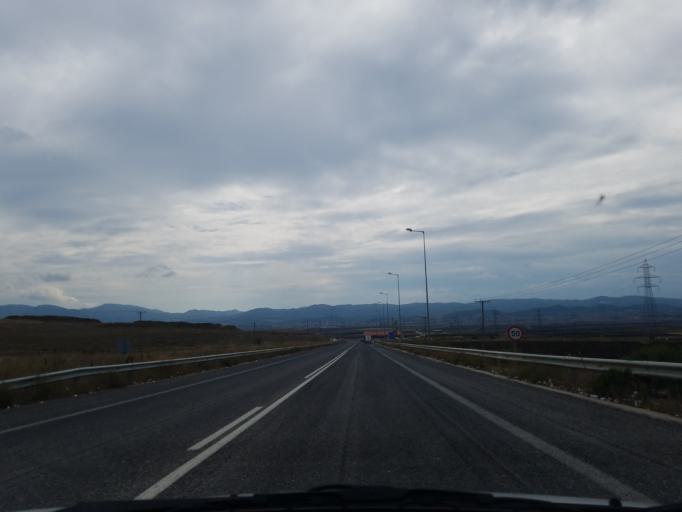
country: GR
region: Central Greece
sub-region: Nomos Fthiotidos
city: Omvriaki
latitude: 39.0884
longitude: 22.3068
